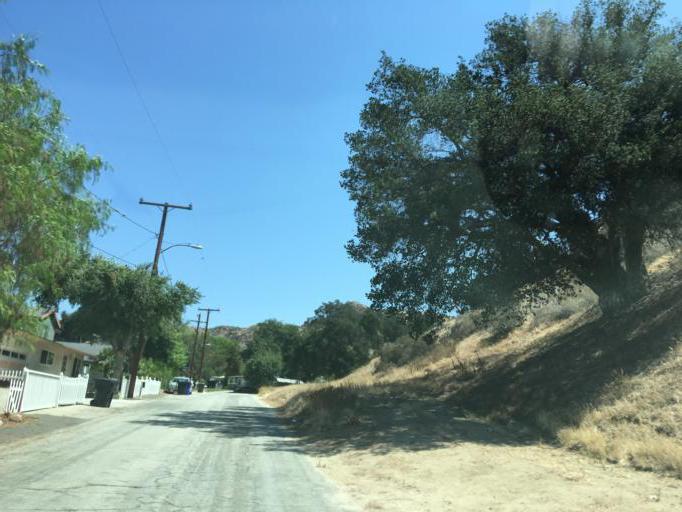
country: US
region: California
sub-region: Los Angeles County
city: Val Verde
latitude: 34.4389
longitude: -118.6564
